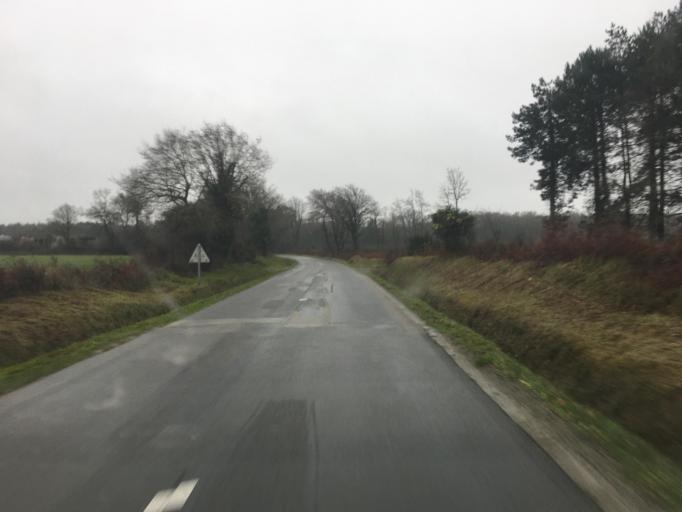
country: FR
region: Brittany
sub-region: Departement du Morbihan
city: Sarzeau
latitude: 47.5247
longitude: -2.6966
